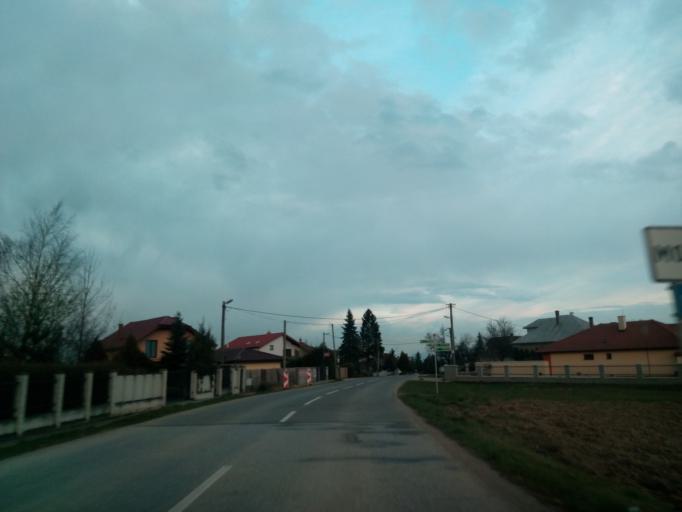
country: SK
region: Kosicky
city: Moldava nad Bodvou
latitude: 48.6006
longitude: 21.0117
